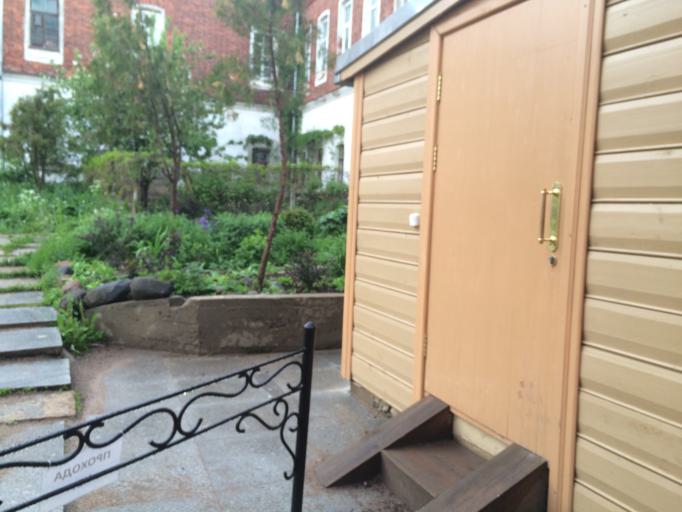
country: RU
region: Republic of Karelia
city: Lyaskelya
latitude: 61.3895
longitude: 30.9457
